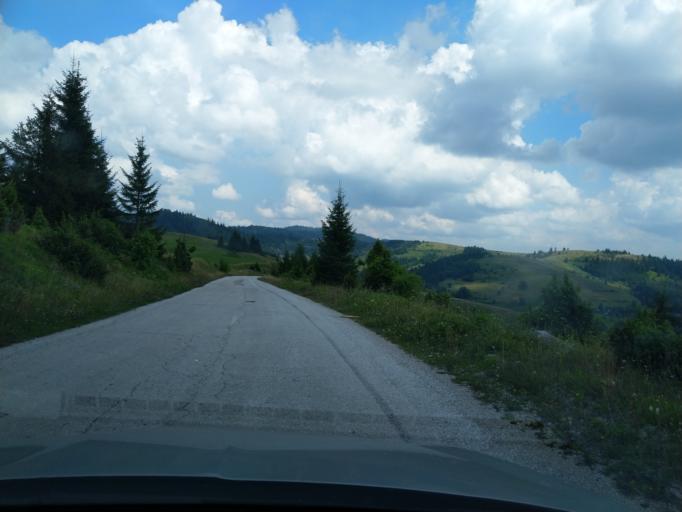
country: RS
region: Central Serbia
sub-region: Zlatiborski Okrug
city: Nova Varos
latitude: 43.5326
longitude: 19.8970
